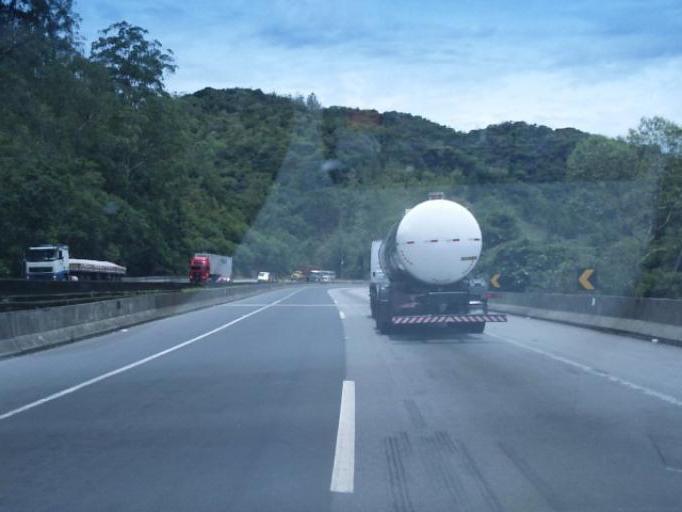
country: BR
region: Sao Paulo
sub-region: Juquitiba
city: Juquitiba
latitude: -24.0432
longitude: -47.1935
